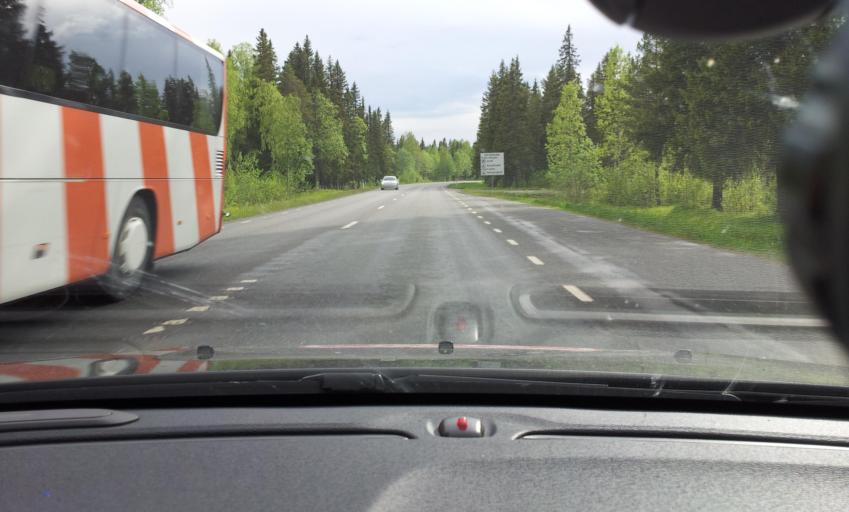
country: SE
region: Jaemtland
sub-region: OEstersunds Kommun
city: Ostersund
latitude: 63.1853
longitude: 14.7306
